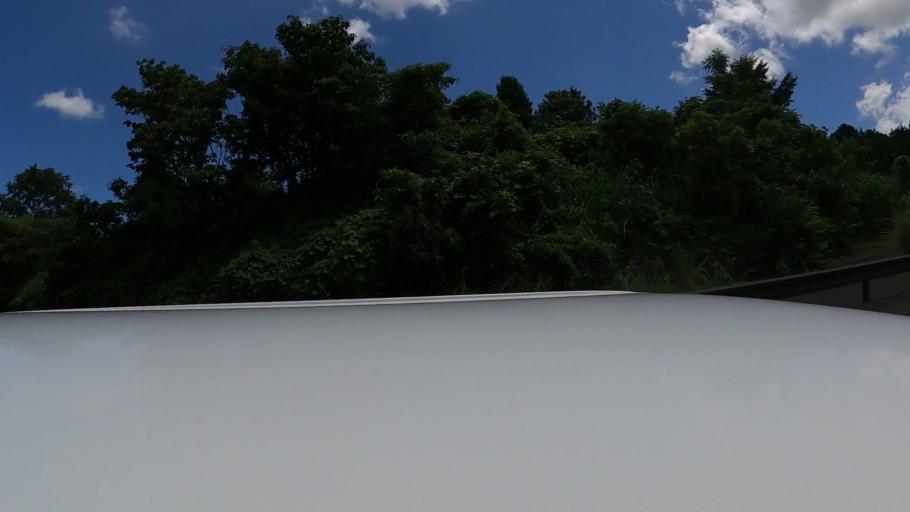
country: JP
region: Miyazaki
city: Nobeoka
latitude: 32.5692
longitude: 131.5573
